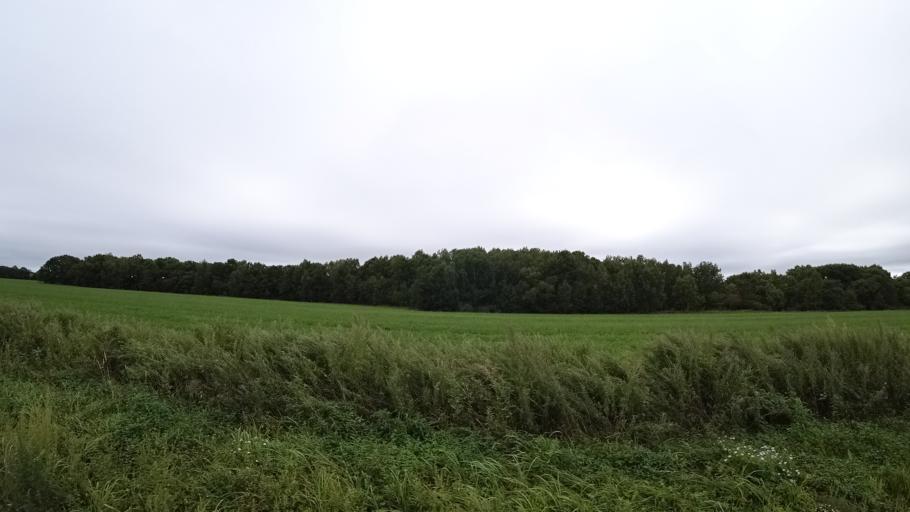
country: RU
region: Primorskiy
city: Rettikhovka
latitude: 44.0695
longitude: 132.6408
